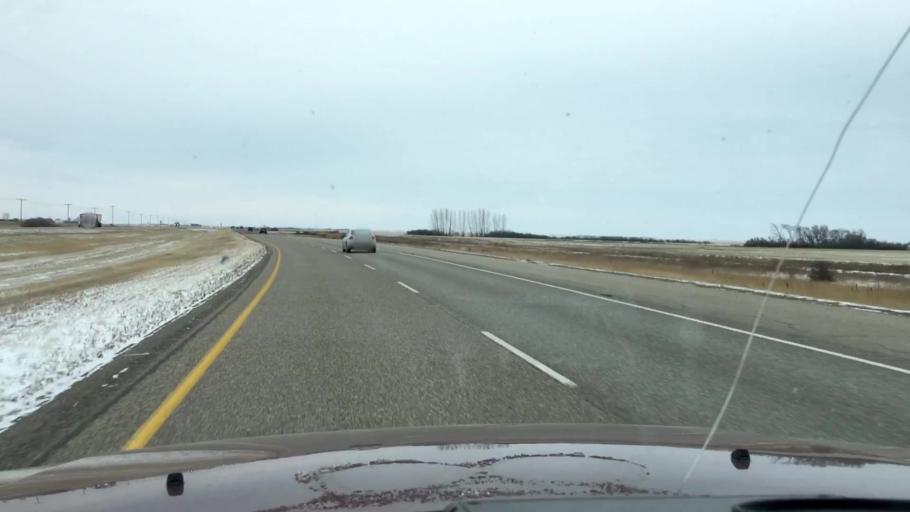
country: CA
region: Saskatchewan
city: Watrous
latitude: 51.1433
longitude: -105.9056
